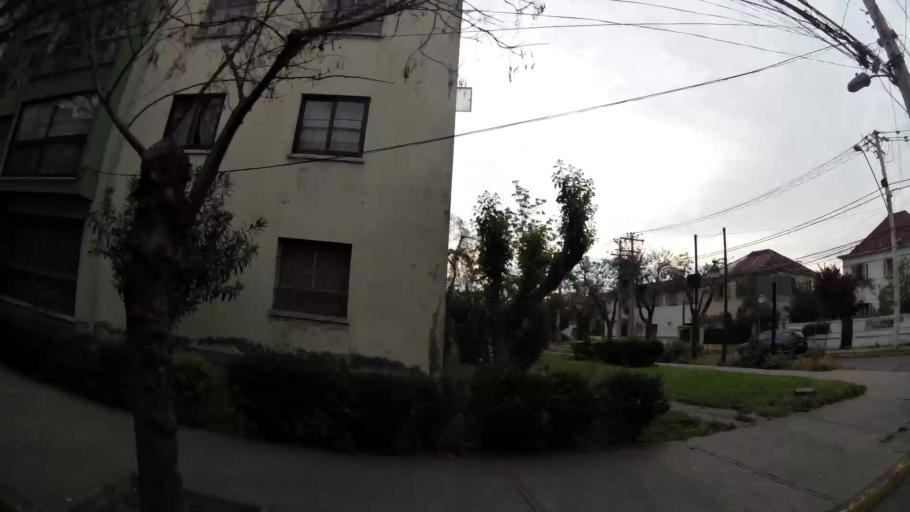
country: CL
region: Santiago Metropolitan
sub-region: Provincia de Santiago
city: Santiago
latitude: -33.4514
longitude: -70.6160
